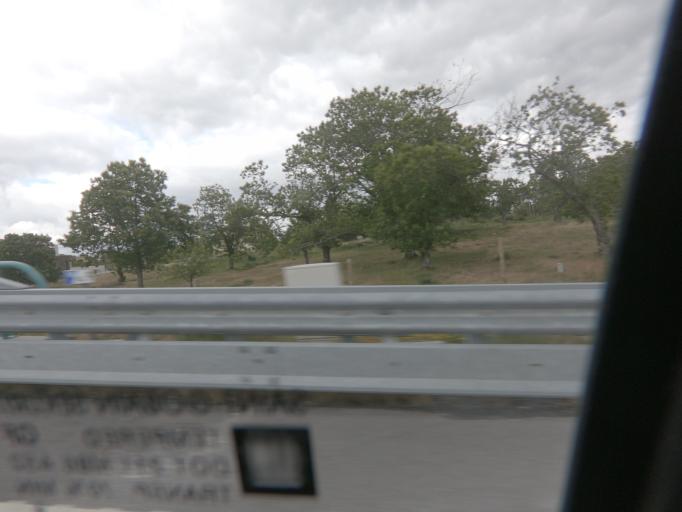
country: PT
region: Vila Real
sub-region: Santa Marta de Penaguiao
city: Santa Marta de Penaguiao
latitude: 41.2701
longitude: -7.8166
